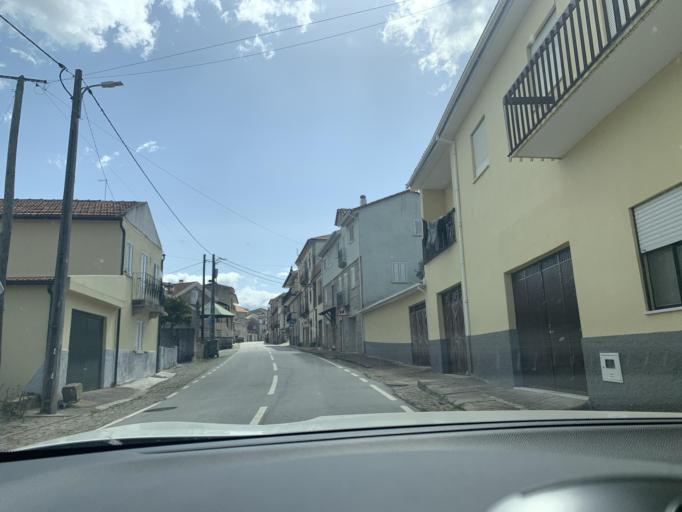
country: PT
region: Guarda
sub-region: Fornos de Algodres
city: Fornos de Algodres
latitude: 40.5696
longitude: -7.5824
